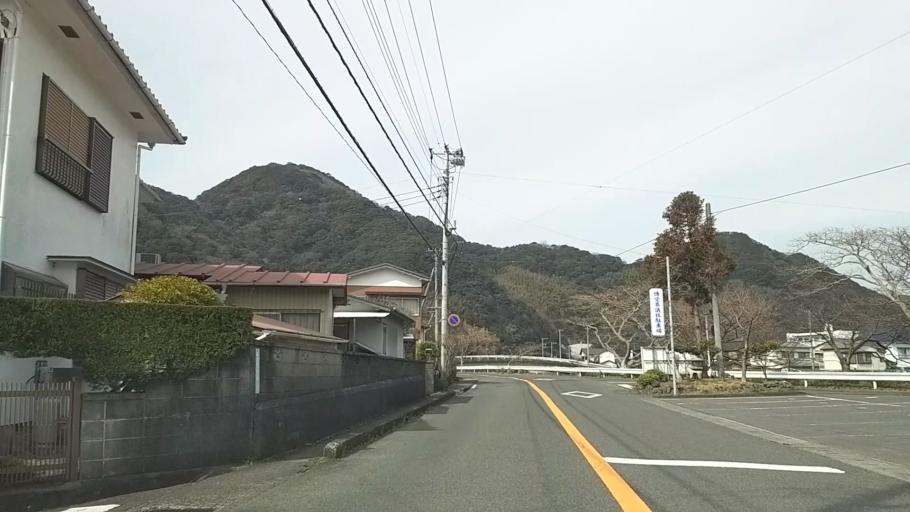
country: JP
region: Shizuoka
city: Shimoda
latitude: 34.6866
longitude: 138.9433
